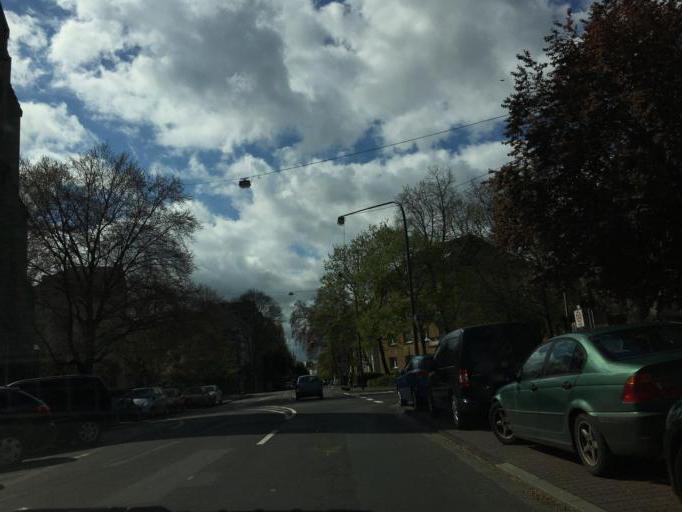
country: DE
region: Hesse
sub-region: Regierungsbezirk Darmstadt
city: Frankfurt am Main
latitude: 50.1289
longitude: 8.6834
